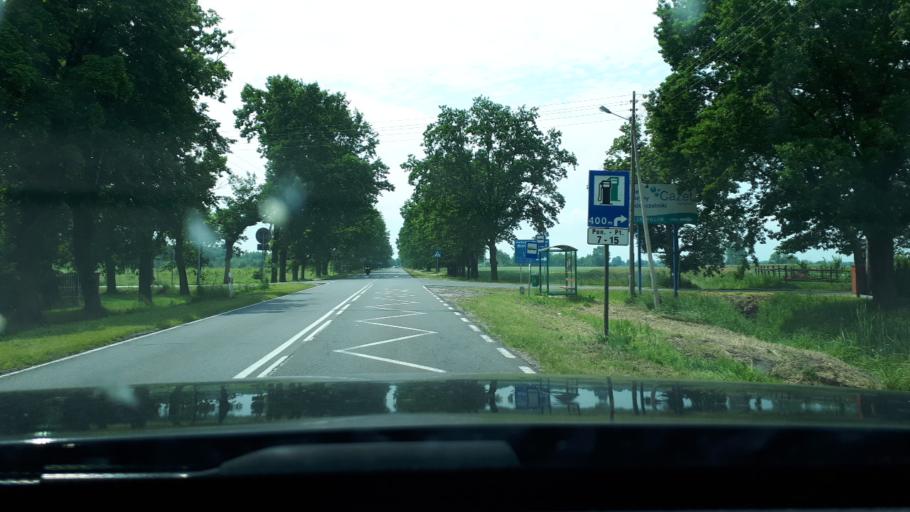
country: PL
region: Masovian Voivodeship
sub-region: Powiat warszawski zachodni
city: Kampinos
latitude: 52.2694
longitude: 20.3969
